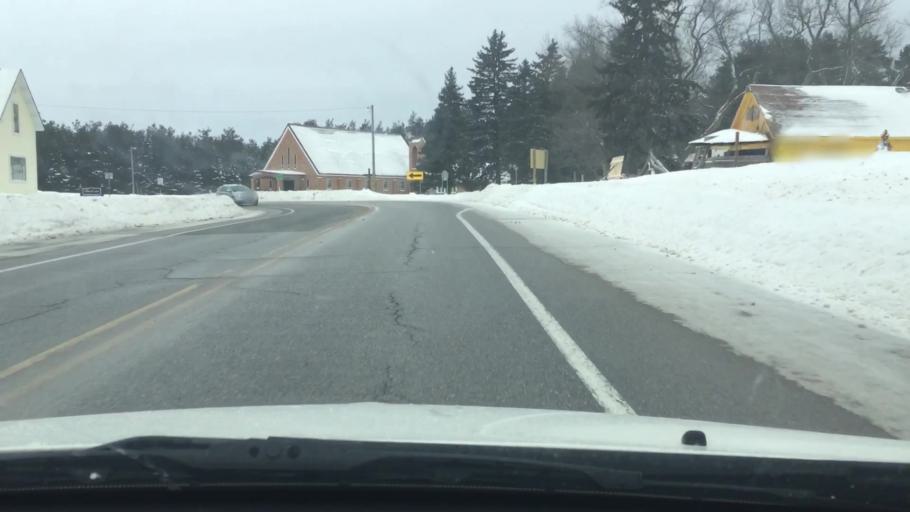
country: US
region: Michigan
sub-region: Otsego County
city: Gaylord
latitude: 45.0657
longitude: -84.8575
